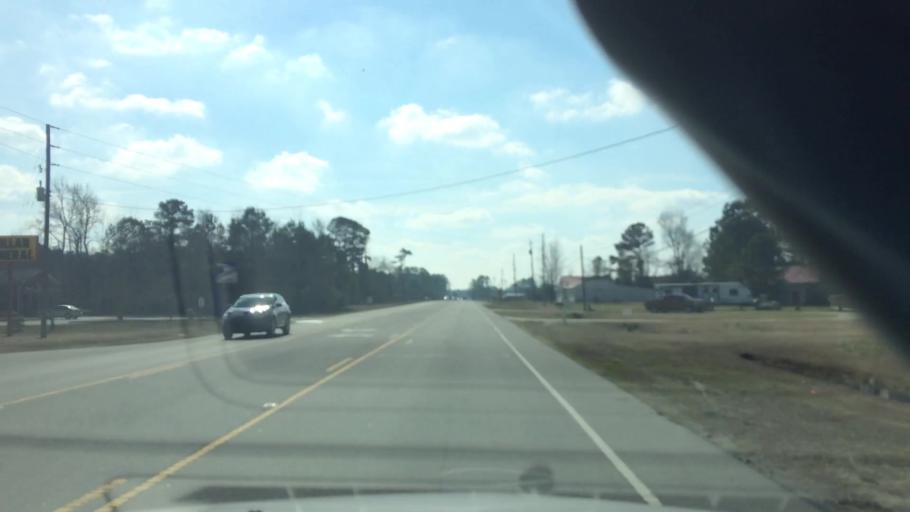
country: US
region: North Carolina
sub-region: Duplin County
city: Beulaville
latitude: 35.0754
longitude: -77.7344
